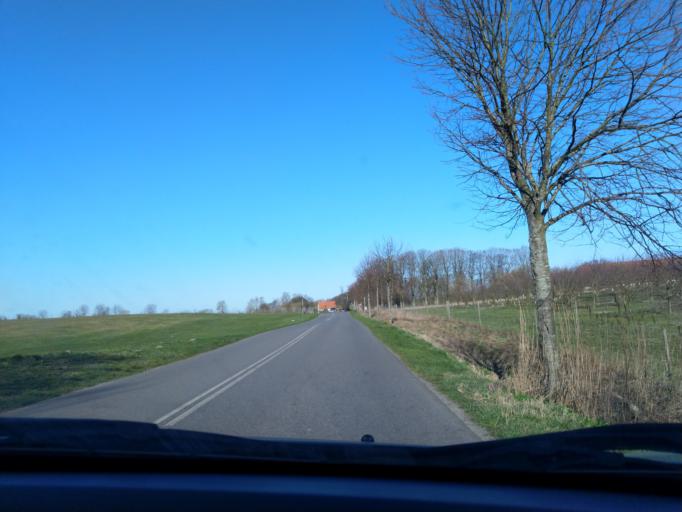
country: DK
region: Zealand
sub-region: Kalundborg Kommune
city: Kalundborg
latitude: 55.7312
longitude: 10.9820
